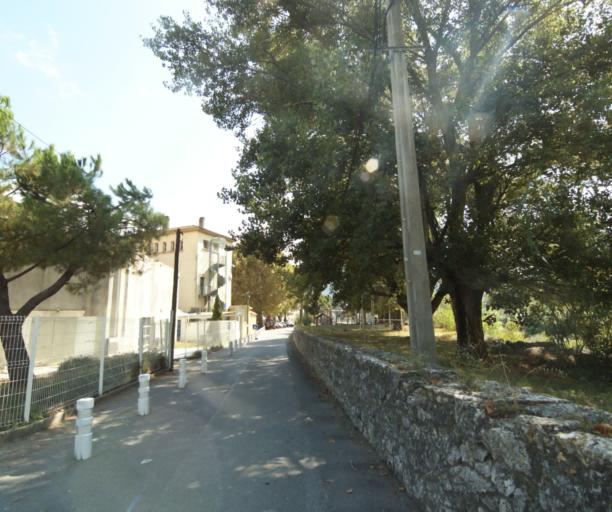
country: FR
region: Provence-Alpes-Cote d'Azur
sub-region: Departement des Alpes-Maritimes
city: Drap
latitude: 43.7562
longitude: 7.3196
